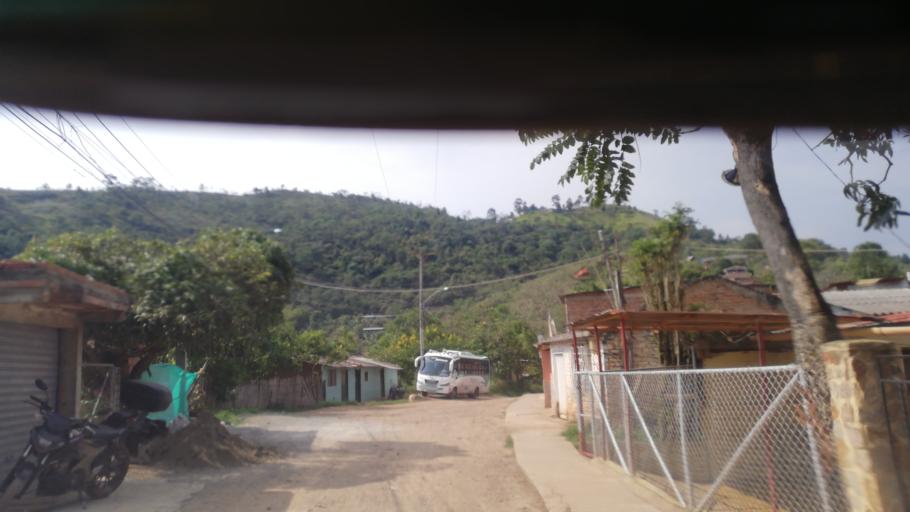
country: CO
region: Valle del Cauca
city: Cali
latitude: 3.4998
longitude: -76.5480
